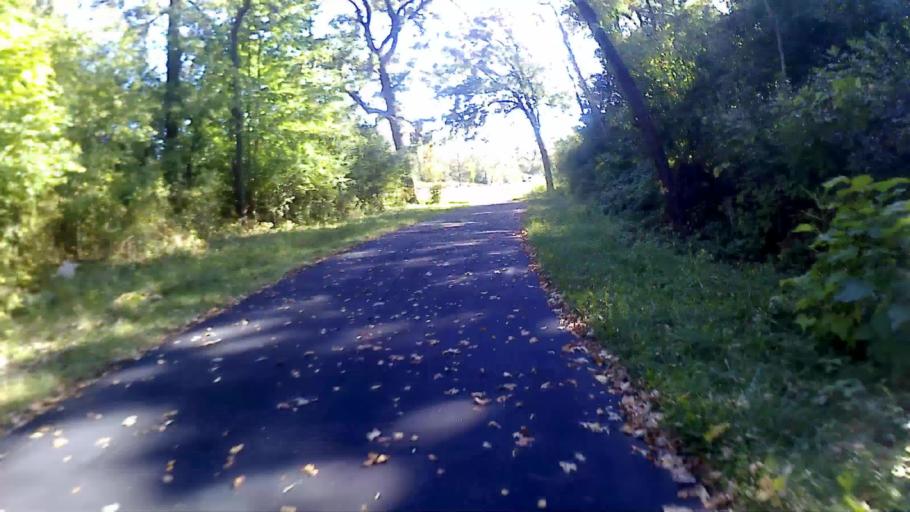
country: US
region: Illinois
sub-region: DuPage County
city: Addison
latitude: 41.9307
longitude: -87.9781
